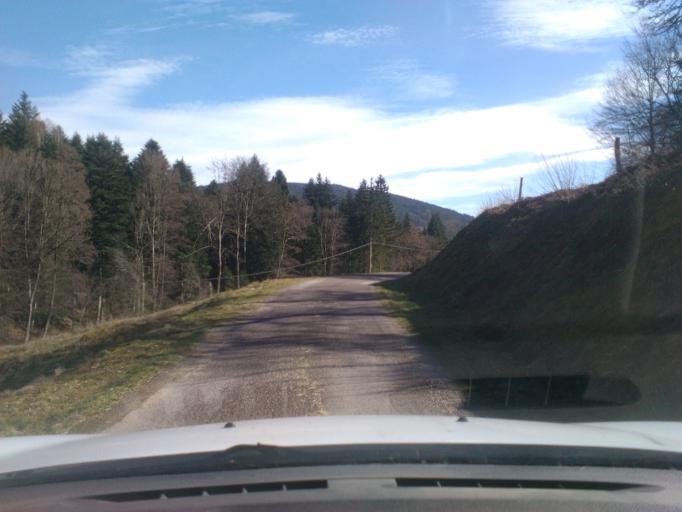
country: FR
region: Lorraine
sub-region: Departement des Vosges
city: Saint-Ame
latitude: 48.0444
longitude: 6.6651
